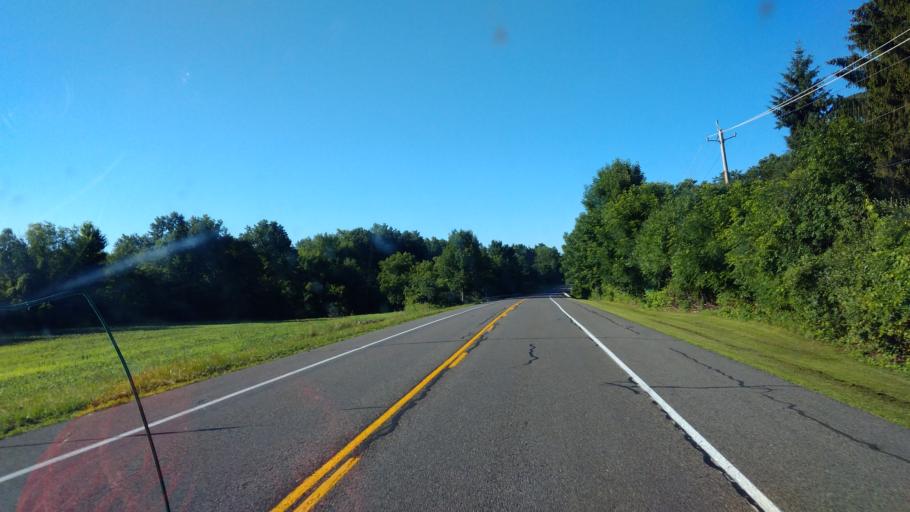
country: US
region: New York
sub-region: Ontario County
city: Phelps
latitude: 42.9818
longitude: -76.9782
